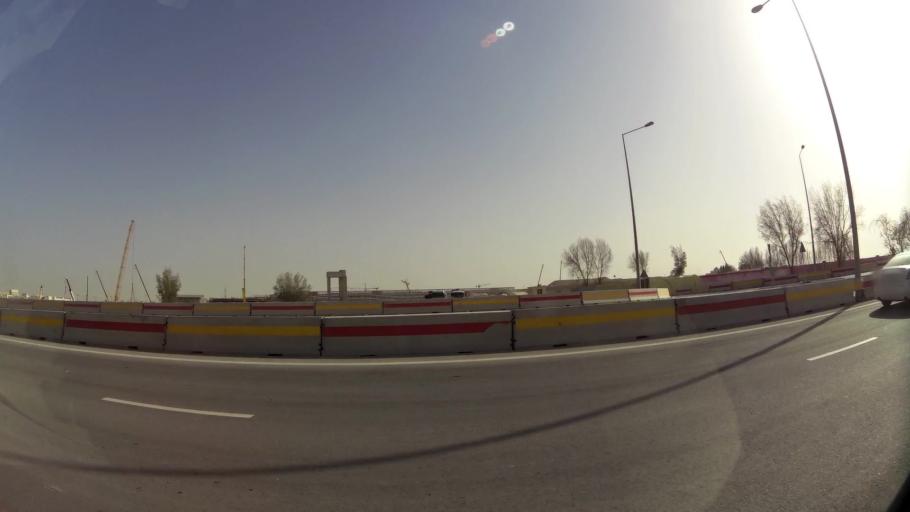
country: QA
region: Baladiyat ar Rayyan
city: Ar Rayyan
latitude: 25.3192
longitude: 51.4240
